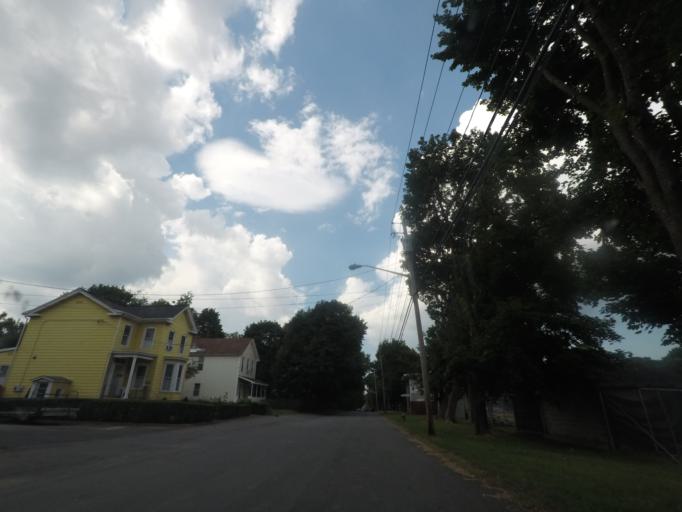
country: US
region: New York
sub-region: Rensselaer County
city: Troy
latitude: 42.7060
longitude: -73.6891
